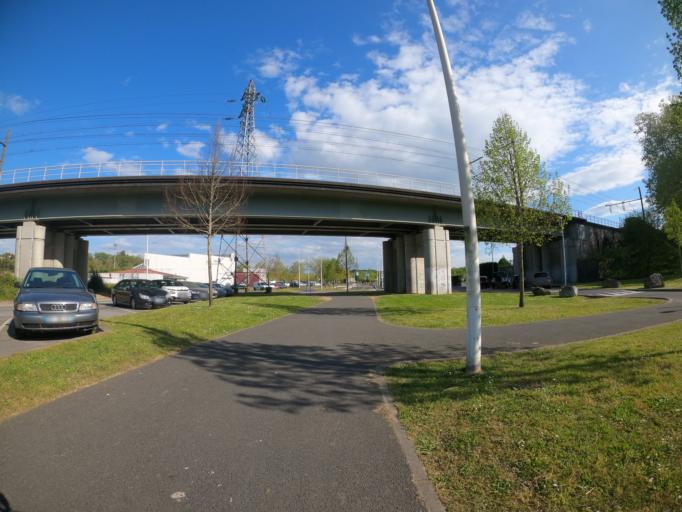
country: FR
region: Aquitaine
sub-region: Departement des Pyrenees-Atlantiques
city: Bayonne
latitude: 43.4799
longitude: -1.4746
